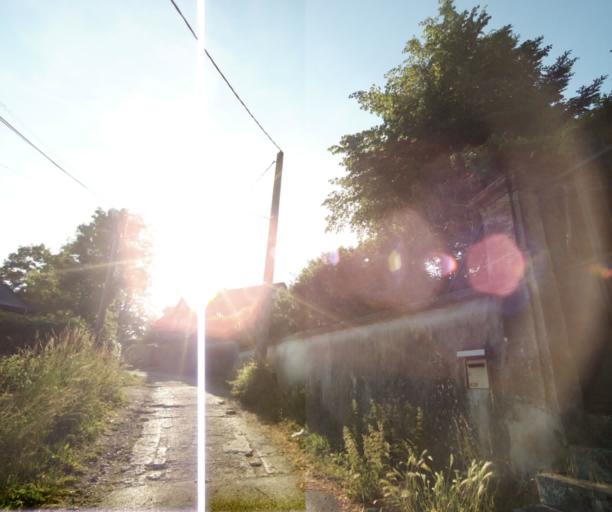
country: FR
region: Champagne-Ardenne
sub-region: Departement des Ardennes
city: Charleville-Mezieres
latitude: 49.7841
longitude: 4.7180
